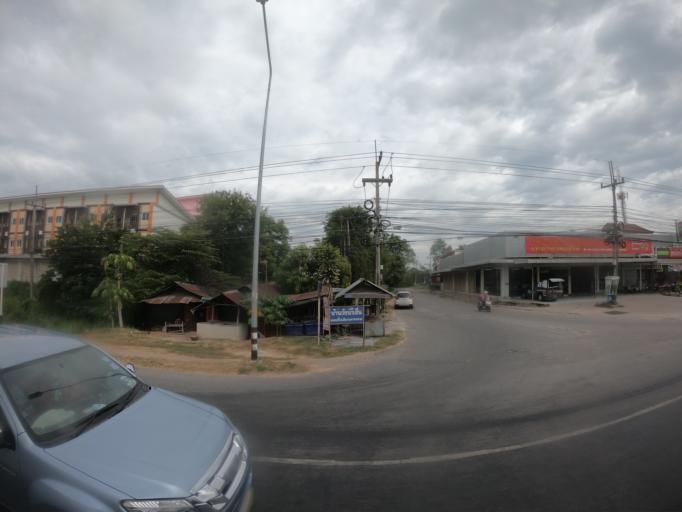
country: TH
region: Maha Sarakham
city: Maha Sarakham
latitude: 16.2072
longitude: 103.2858
